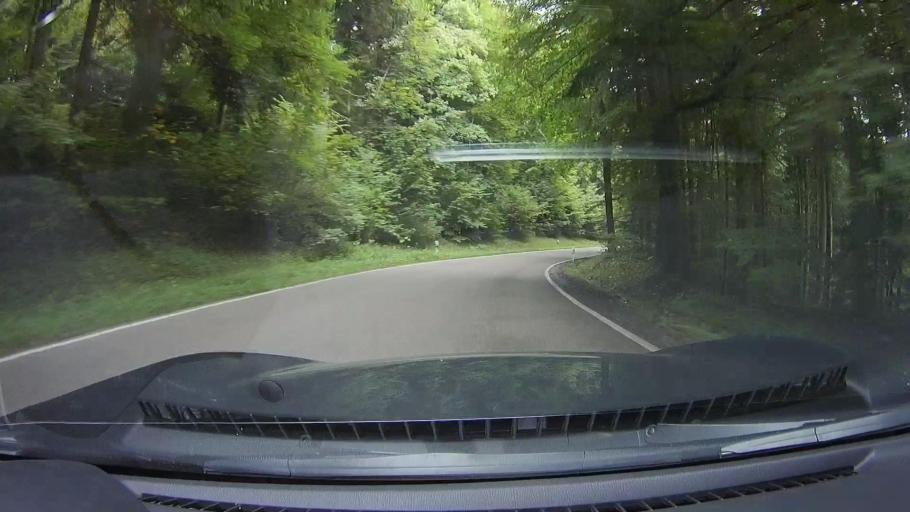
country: DE
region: Baden-Wuerttemberg
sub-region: Regierungsbezirk Stuttgart
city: Kaisersbach
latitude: 48.9476
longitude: 9.6307
